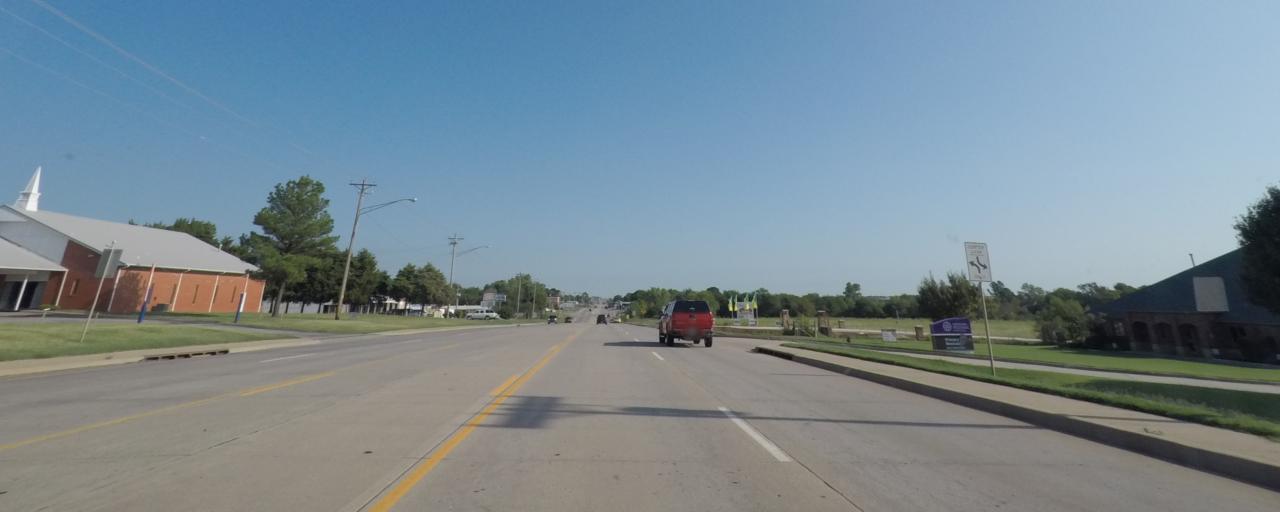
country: US
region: Oklahoma
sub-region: McClain County
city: Newcastle
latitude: 35.2437
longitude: -97.6002
